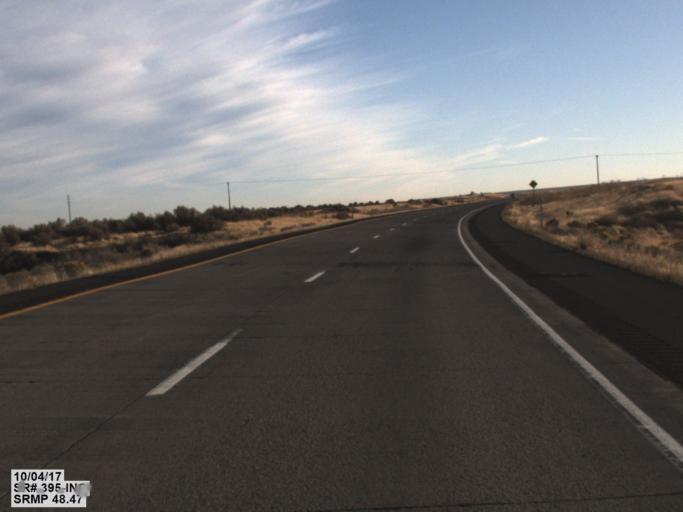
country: US
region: Washington
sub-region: Franklin County
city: Connell
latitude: 46.5937
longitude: -118.9550
